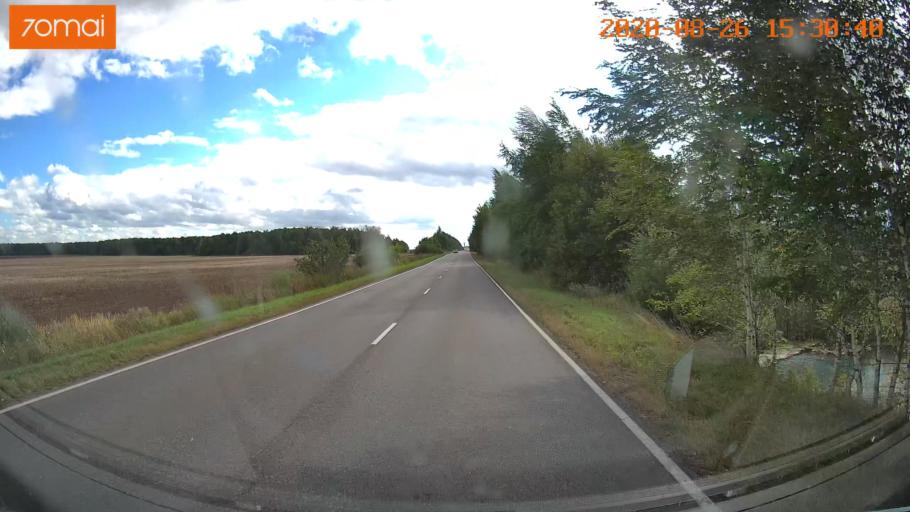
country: RU
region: Tula
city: Severo-Zadonsk
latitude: 54.0889
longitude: 38.3951
